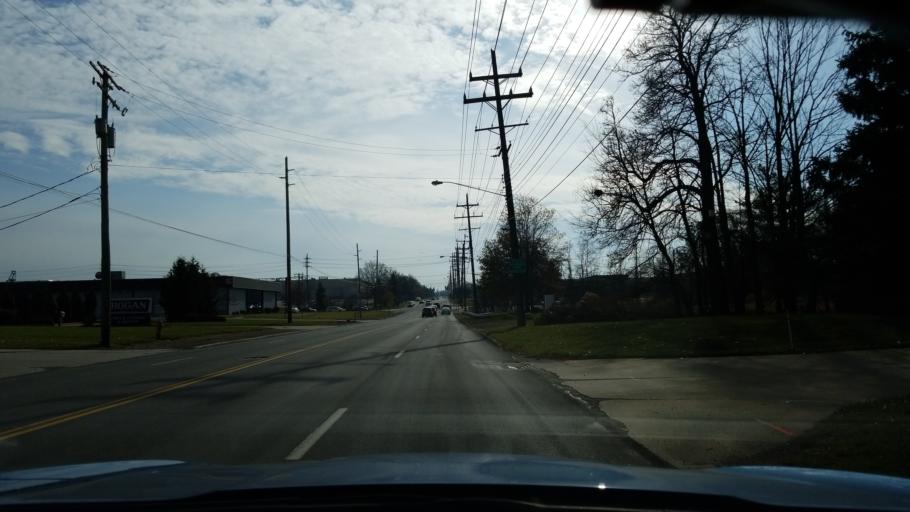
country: US
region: Ohio
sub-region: Summit County
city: Northfield
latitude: 41.3600
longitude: -81.5268
